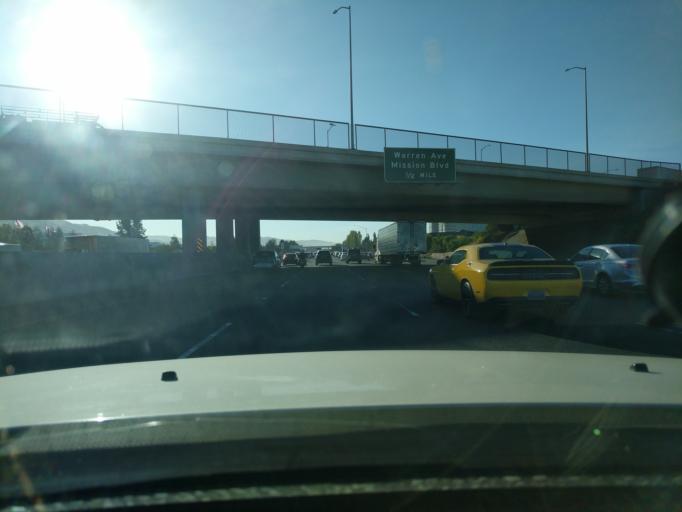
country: US
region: California
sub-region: Alameda County
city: Fremont
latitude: 37.4929
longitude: -121.9491
